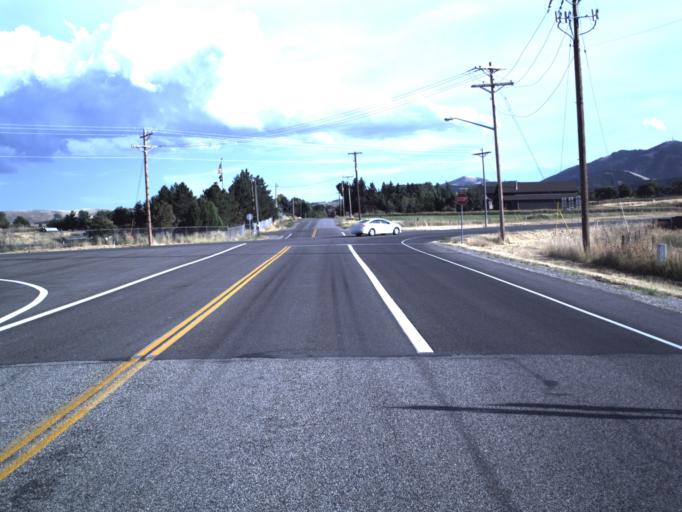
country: US
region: Utah
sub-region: Cache County
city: Wellsville
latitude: 41.6168
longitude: -111.9338
